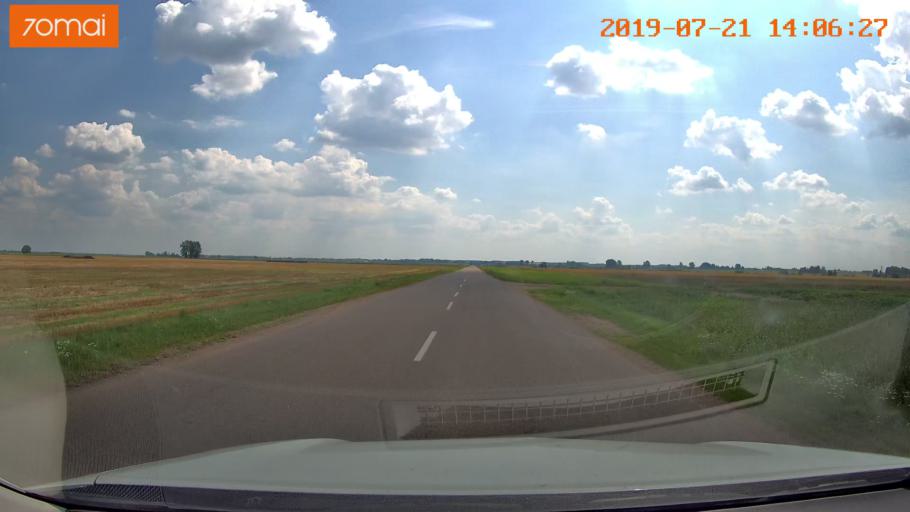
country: BY
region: Grodnenskaya
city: Lyubcha
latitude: 53.6970
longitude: 26.1128
